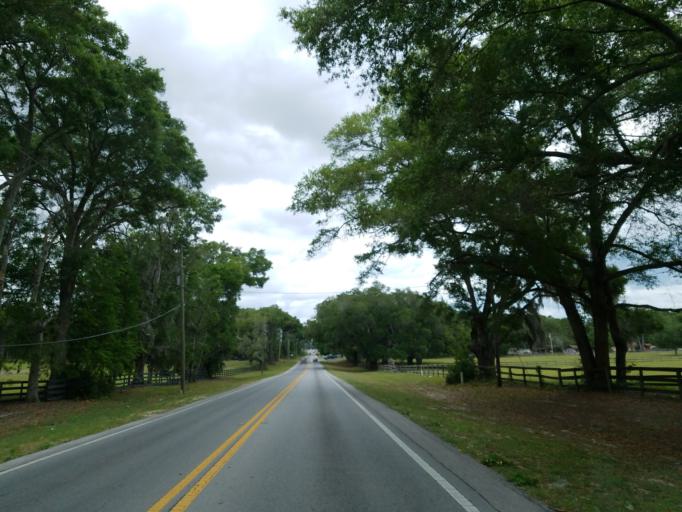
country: US
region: Florida
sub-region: Marion County
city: Ocala
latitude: 29.2753
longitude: -82.1116
